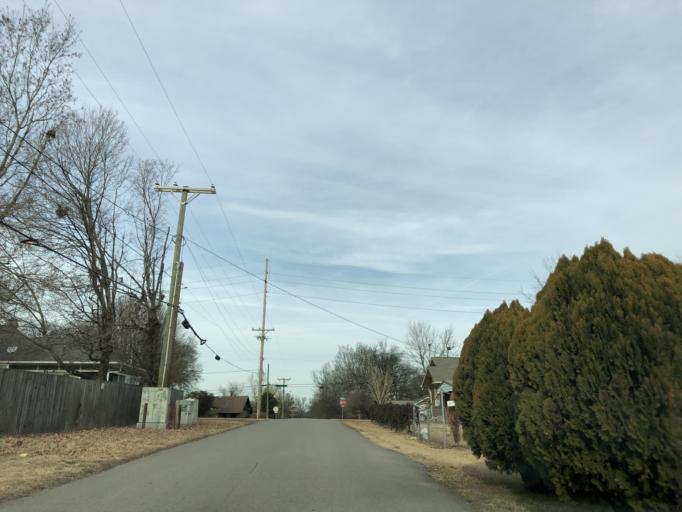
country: US
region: Tennessee
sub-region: Davidson County
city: Nashville
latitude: 36.2108
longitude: -86.7284
